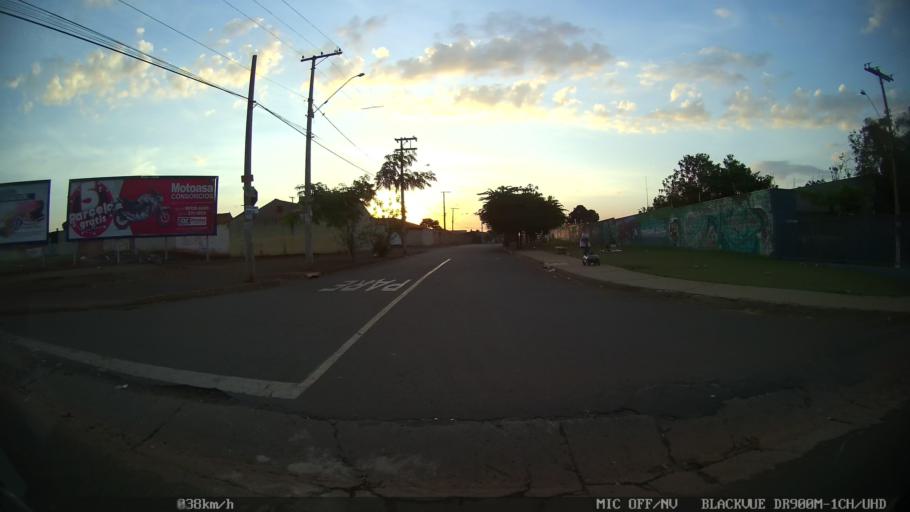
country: BR
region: Sao Paulo
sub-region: Ribeirao Preto
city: Ribeirao Preto
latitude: -21.1366
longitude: -47.8190
